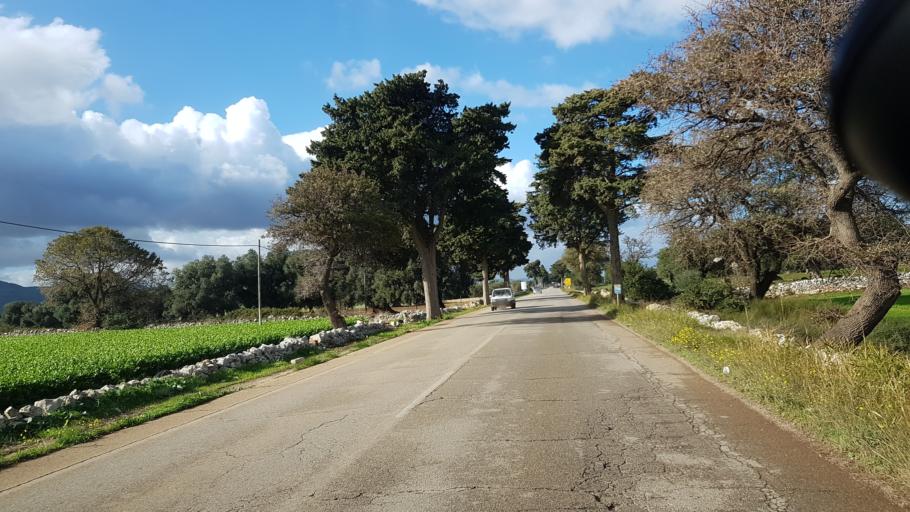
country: IT
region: Apulia
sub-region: Provincia di Brindisi
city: Montalbano
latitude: 40.7850
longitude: 17.4746
